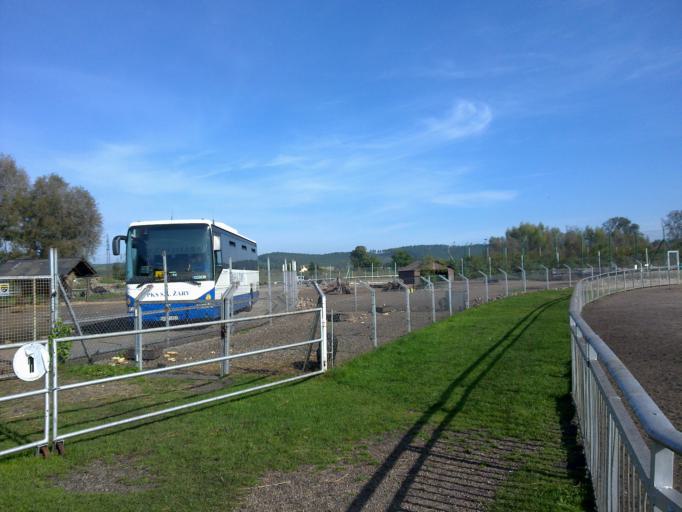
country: PL
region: Lubusz
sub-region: Powiat sulecinski
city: Krzeszyce
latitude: 52.6621
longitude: 14.9930
